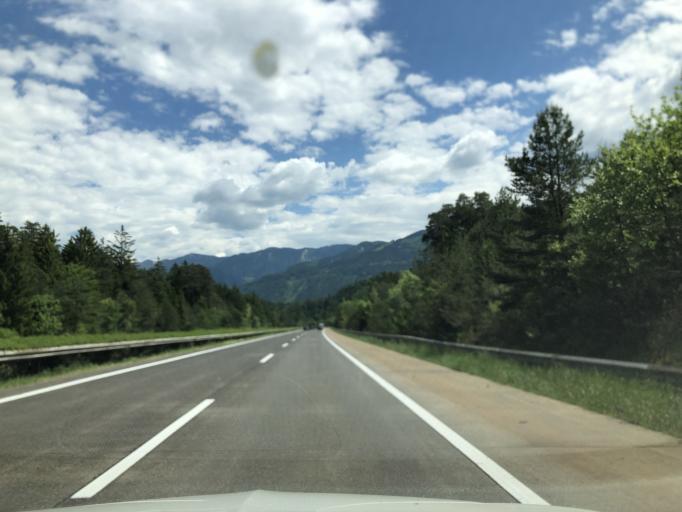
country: AT
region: Carinthia
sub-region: Politischer Bezirk Villach Land
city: Arnoldstein
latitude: 46.5637
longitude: 13.7399
